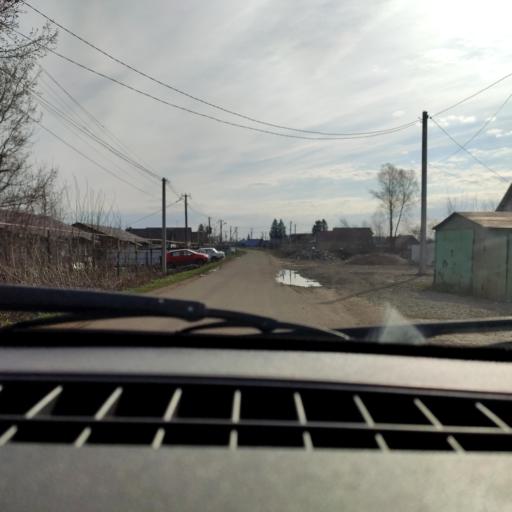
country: RU
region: Bashkortostan
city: Avdon
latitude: 54.6486
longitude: 55.7653
